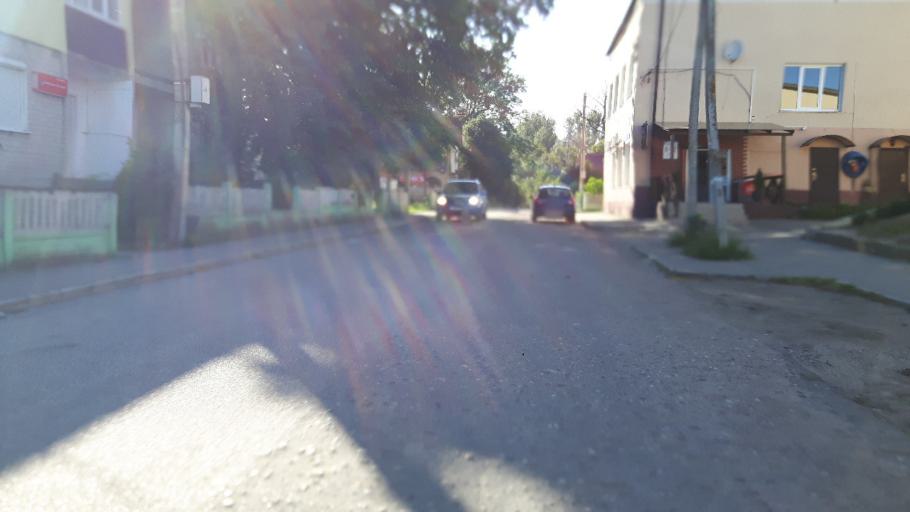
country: LT
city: Nida
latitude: 55.1547
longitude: 20.8522
